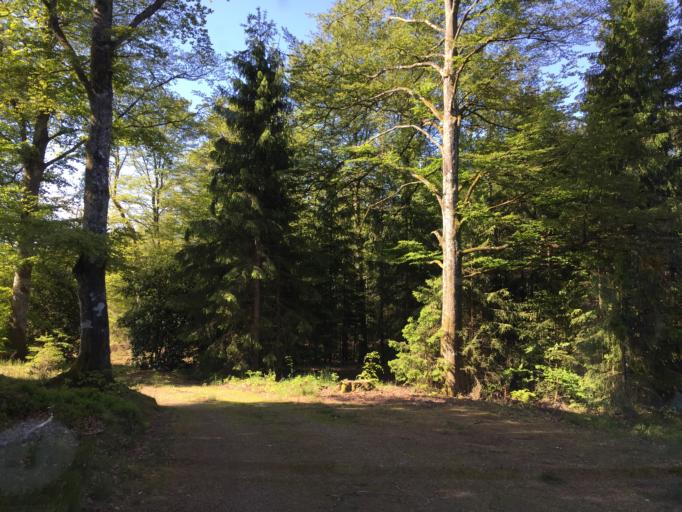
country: SE
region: Kronoberg
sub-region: Markaryds Kommun
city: Markaryd
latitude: 56.5174
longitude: 13.6066
